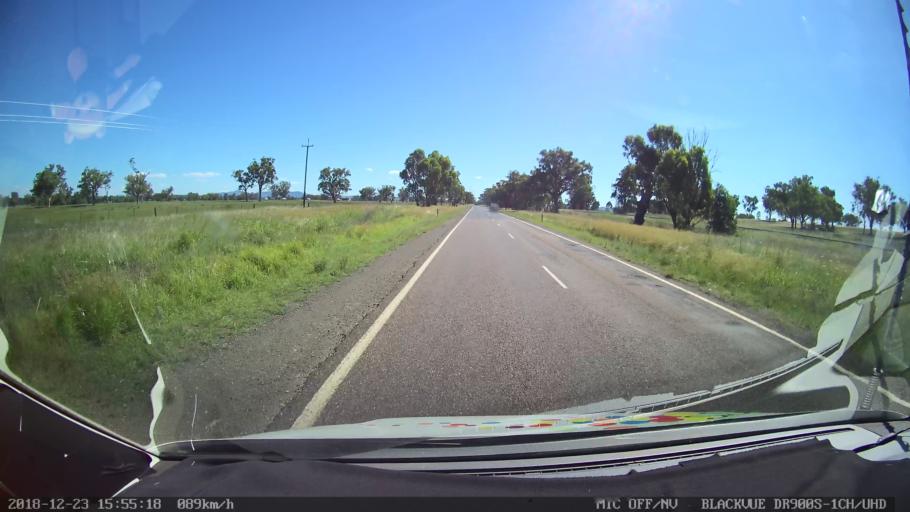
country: AU
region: New South Wales
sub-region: Tamworth Municipality
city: Phillip
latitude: -31.1541
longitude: 150.8698
